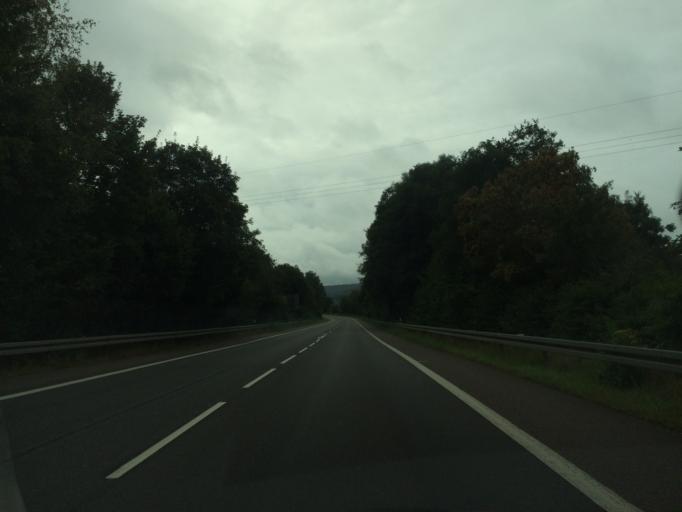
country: DE
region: Saarland
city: Merzig
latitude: 49.4274
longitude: 6.6330
